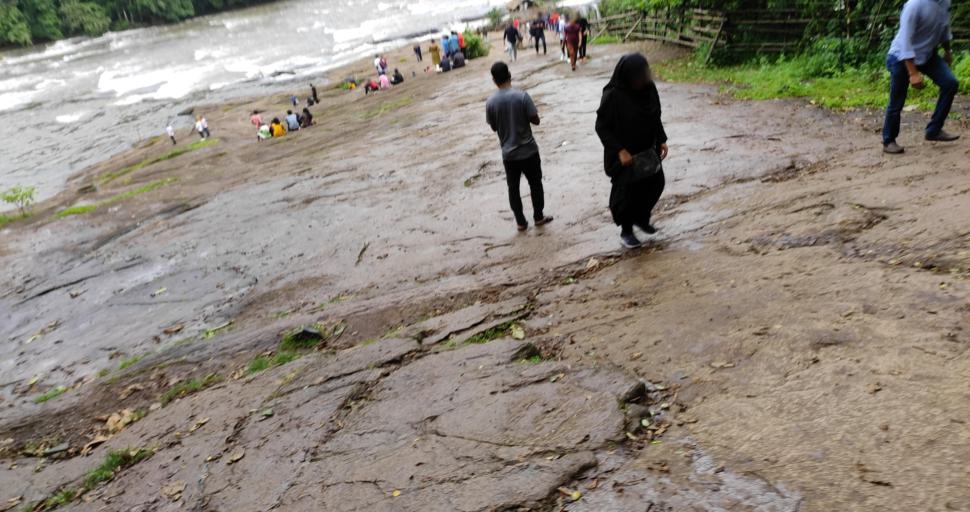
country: IN
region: Kerala
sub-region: Ernakulam
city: Angamali
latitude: 10.2862
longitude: 76.5707
